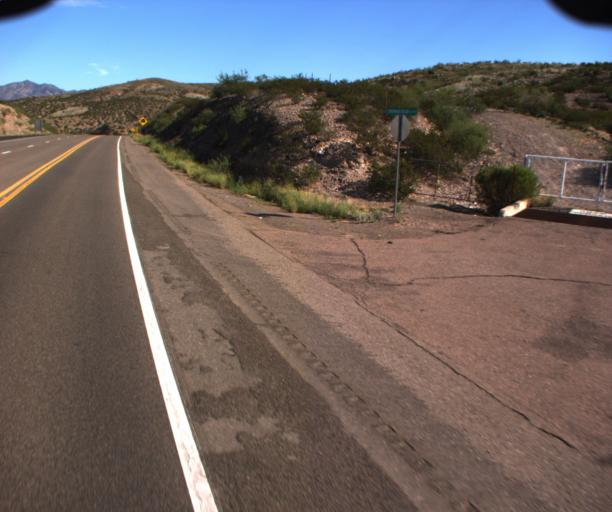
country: US
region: Arizona
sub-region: Greenlee County
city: Clifton
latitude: 33.0093
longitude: -109.2819
